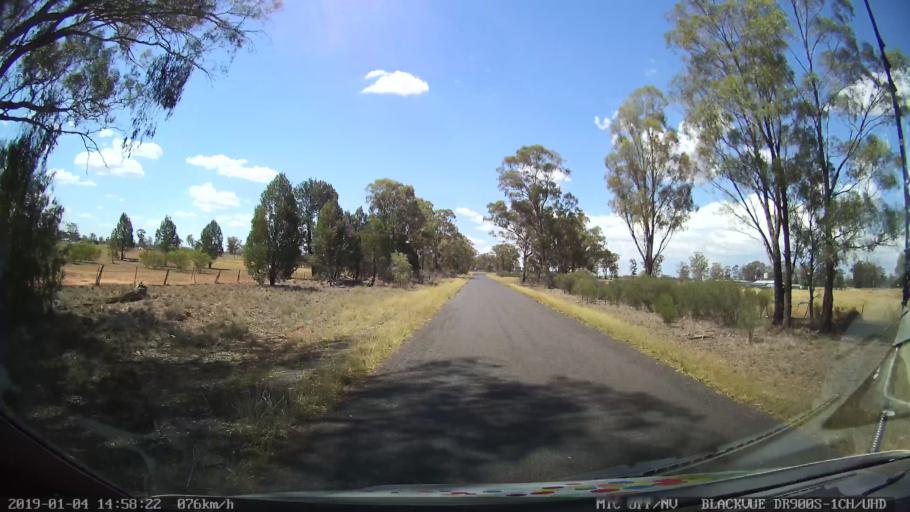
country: AU
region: New South Wales
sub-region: Gilgandra
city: Gilgandra
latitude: -31.9564
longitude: 148.6319
